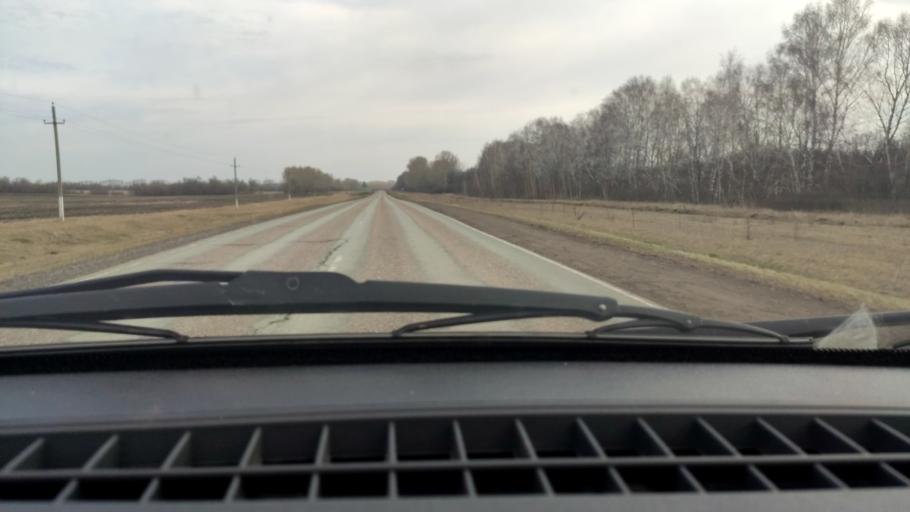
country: RU
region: Bashkortostan
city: Davlekanovo
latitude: 54.3367
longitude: 55.1700
